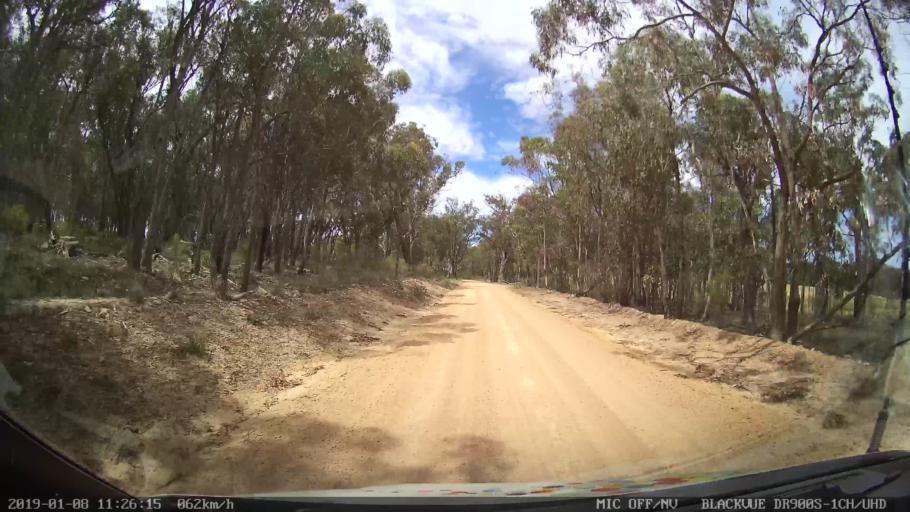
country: AU
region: New South Wales
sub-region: Guyra
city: Guyra
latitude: -30.2790
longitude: 151.5579
